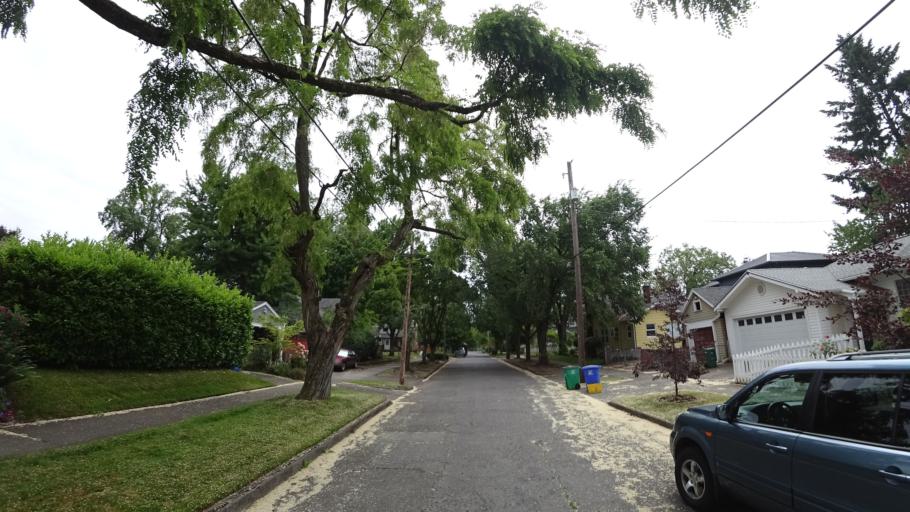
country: US
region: Oregon
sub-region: Multnomah County
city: Portland
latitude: 45.5378
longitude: -122.6076
